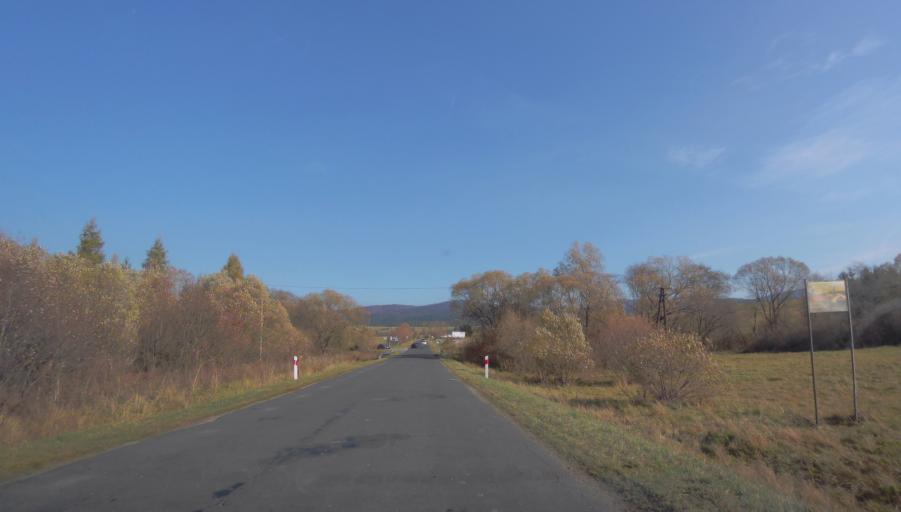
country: PL
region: Subcarpathian Voivodeship
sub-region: Powiat sanocki
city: Komancza
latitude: 49.2456
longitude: 22.1157
